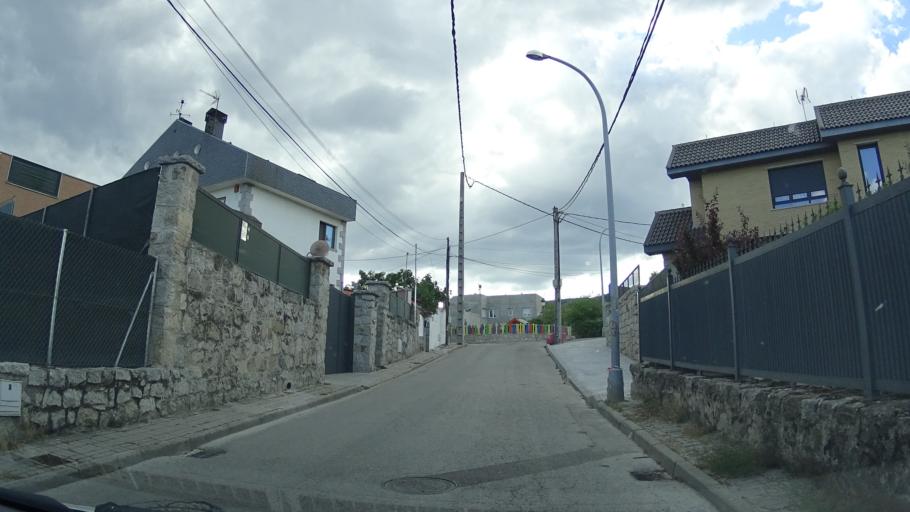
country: ES
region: Madrid
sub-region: Provincia de Madrid
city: Hoyo de Manzanares
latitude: 40.6240
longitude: -3.9024
